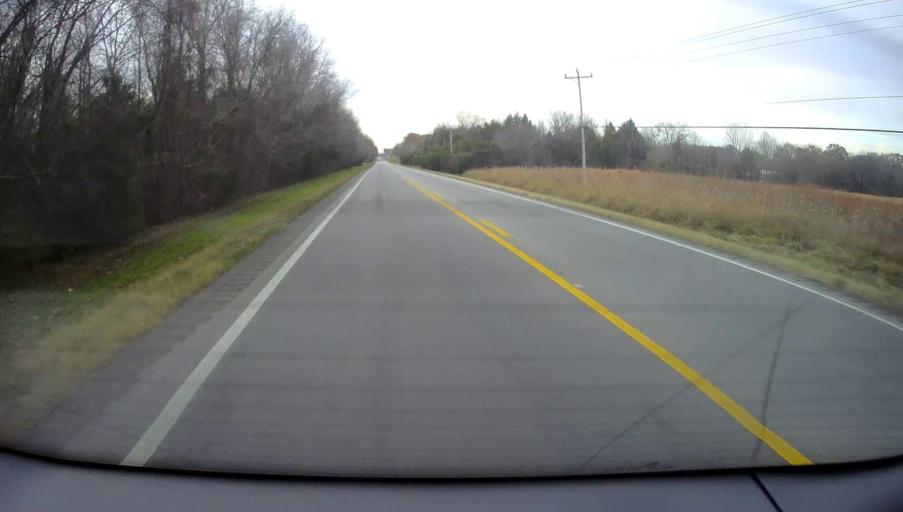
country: US
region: Alabama
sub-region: Morgan County
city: Priceville
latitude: 34.4387
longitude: -86.7446
